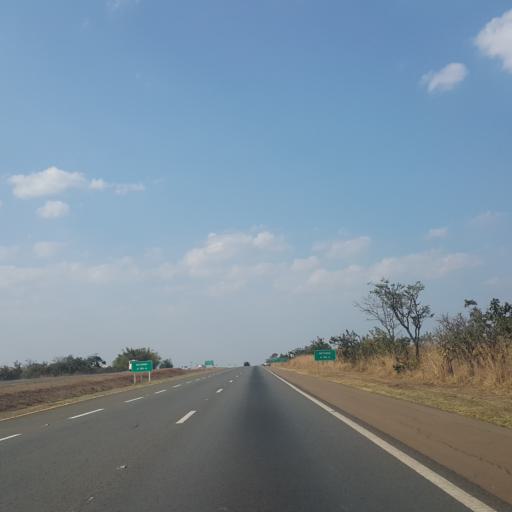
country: BR
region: Goias
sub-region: Abadiania
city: Abadiania
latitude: -16.1968
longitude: -48.7316
